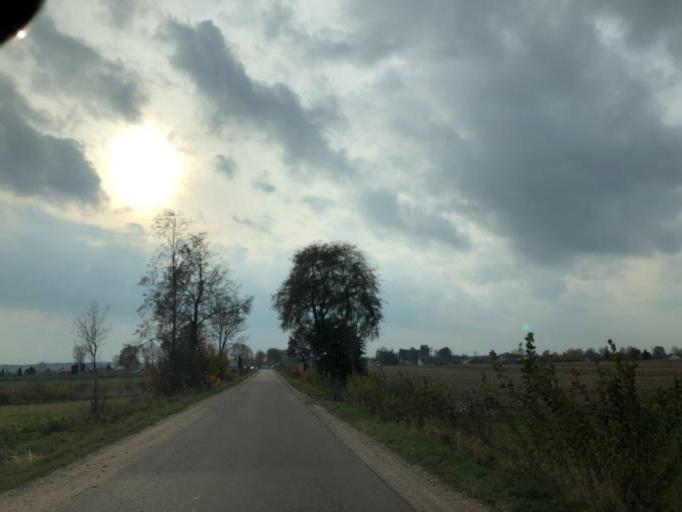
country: PL
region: Podlasie
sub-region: Powiat lomzynski
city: Sniadowo
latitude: 53.1228
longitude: 21.9595
